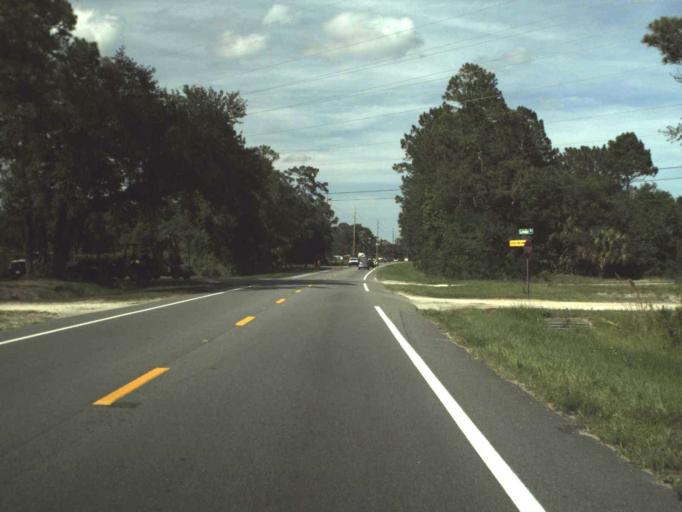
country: US
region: Florida
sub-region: Volusia County
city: West DeLand
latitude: 29.0158
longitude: -81.3740
